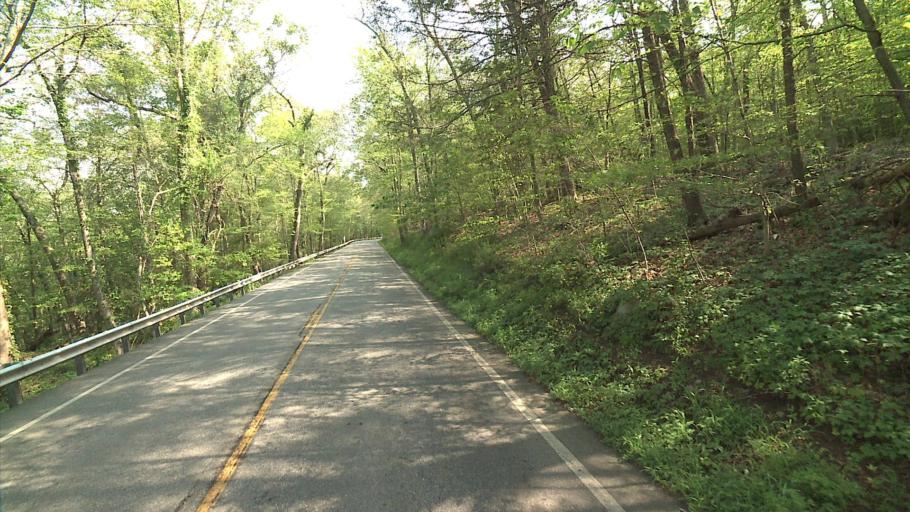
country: US
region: Connecticut
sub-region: Middlesex County
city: East Haddam
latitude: 41.4767
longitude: -72.4692
